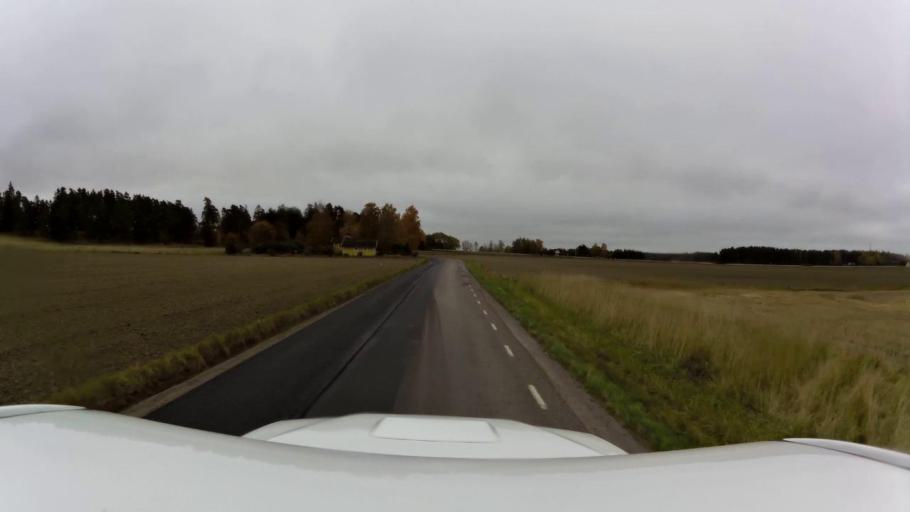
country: SE
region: OEstergoetland
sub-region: Linkopings Kommun
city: Linghem
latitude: 58.4337
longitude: 15.7184
